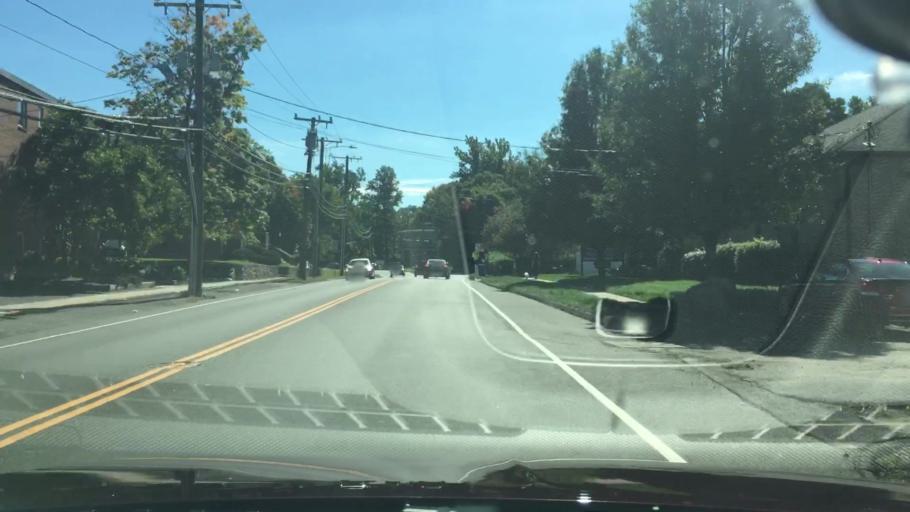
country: US
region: Connecticut
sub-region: Hartford County
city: Plainville
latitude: 41.6786
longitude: -72.9034
